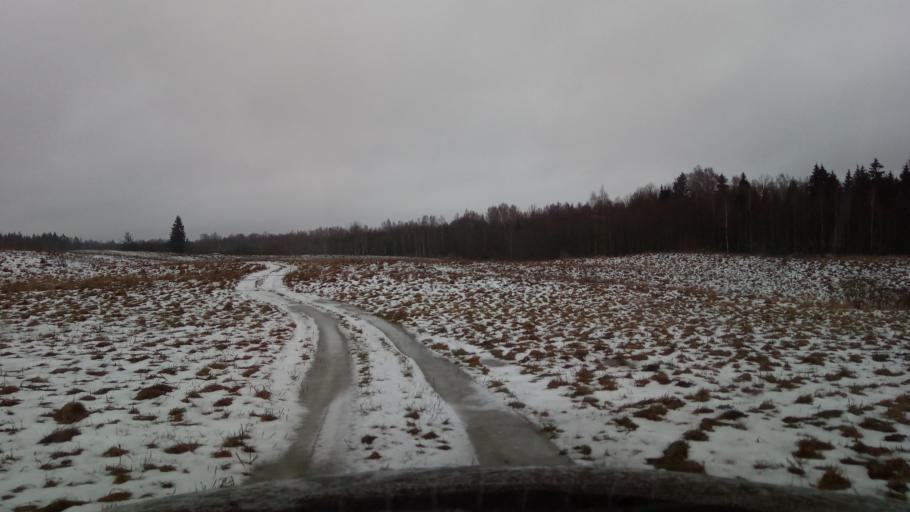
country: LT
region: Utenos apskritis
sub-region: Utena
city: Utena
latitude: 55.3650
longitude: 25.8093
